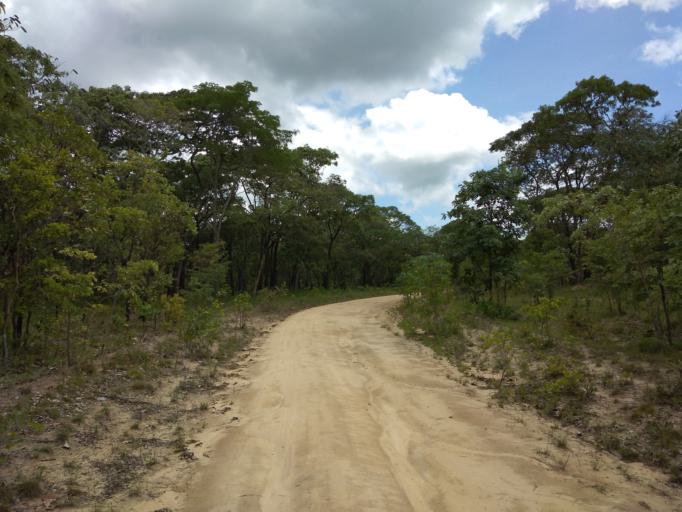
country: ZM
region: Central
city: Mkushi
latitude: -14.0259
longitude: 29.9646
